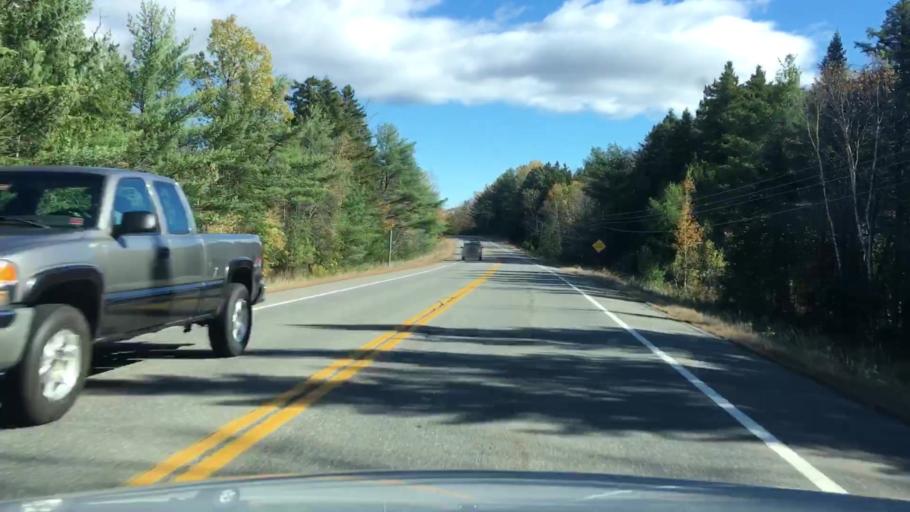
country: US
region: Maine
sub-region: Penobscot County
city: Millinocket
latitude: 45.6570
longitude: -68.6544
